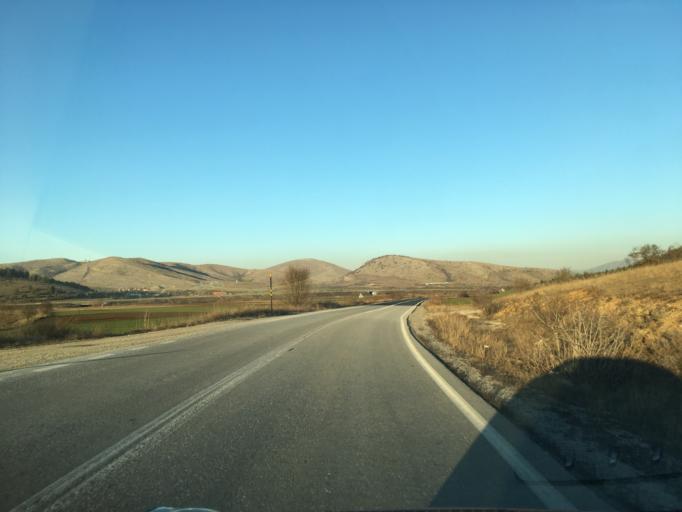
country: GR
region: West Macedonia
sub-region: Nomos Kozanis
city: Kozani
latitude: 40.3136
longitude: 21.7327
